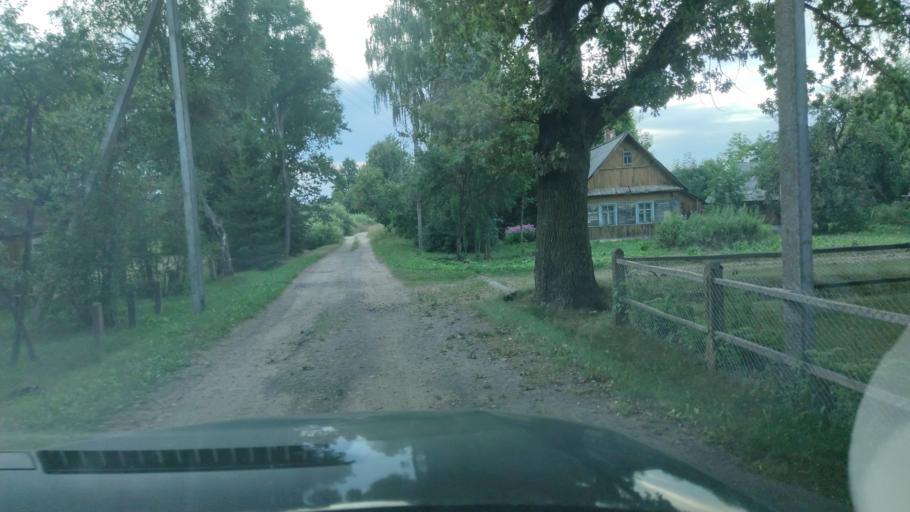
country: BY
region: Vitebsk
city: Mosar
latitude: 55.1243
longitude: 27.1730
